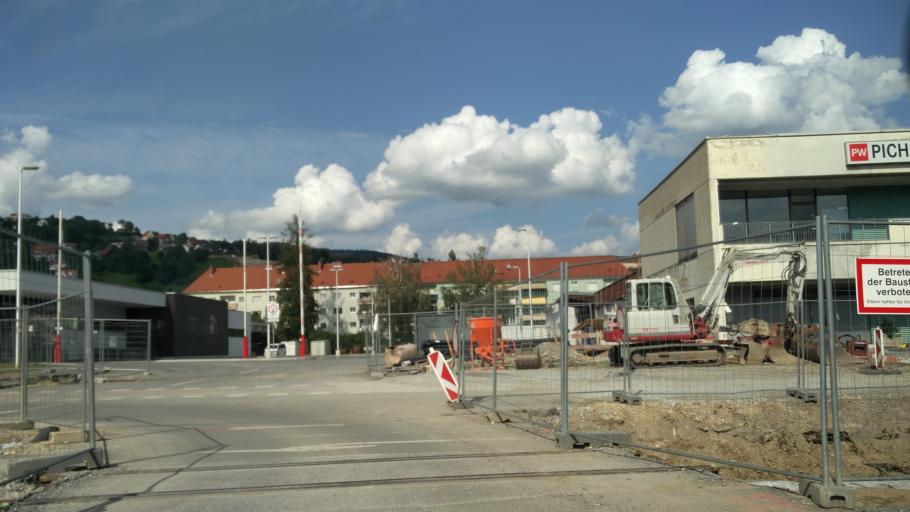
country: AT
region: Styria
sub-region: Politischer Bezirk Weiz
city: Weiz
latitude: 47.2209
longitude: 15.6250
